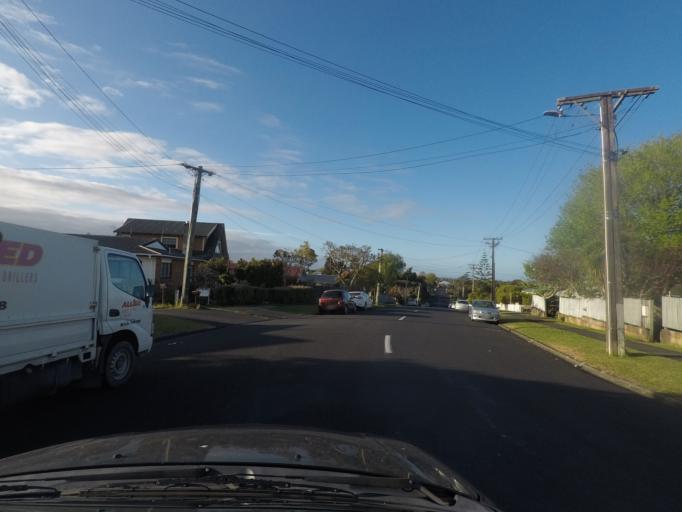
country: NZ
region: Auckland
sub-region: Auckland
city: Waitakere
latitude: -36.9087
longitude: 174.6727
